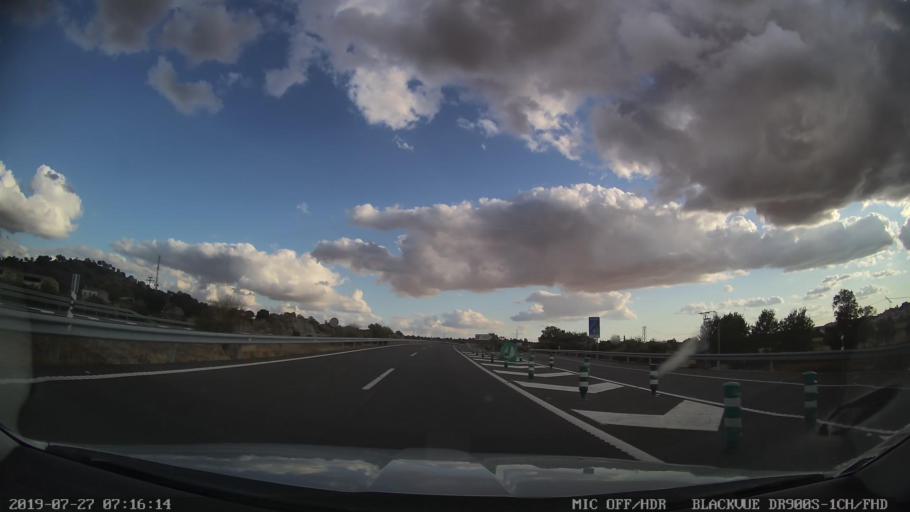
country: ES
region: Extremadura
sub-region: Provincia de Caceres
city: Trujillo
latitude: 39.4595
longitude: -5.8610
